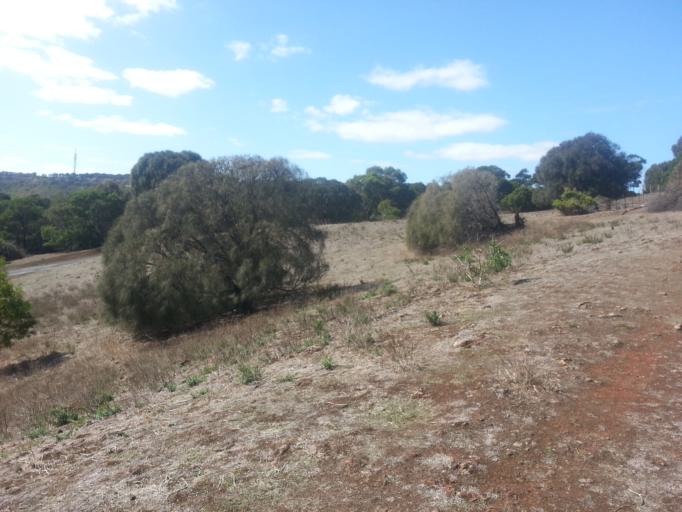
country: AU
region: Victoria
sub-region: Warrnambool
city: Warrnambool
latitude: -38.3213
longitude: 142.3633
